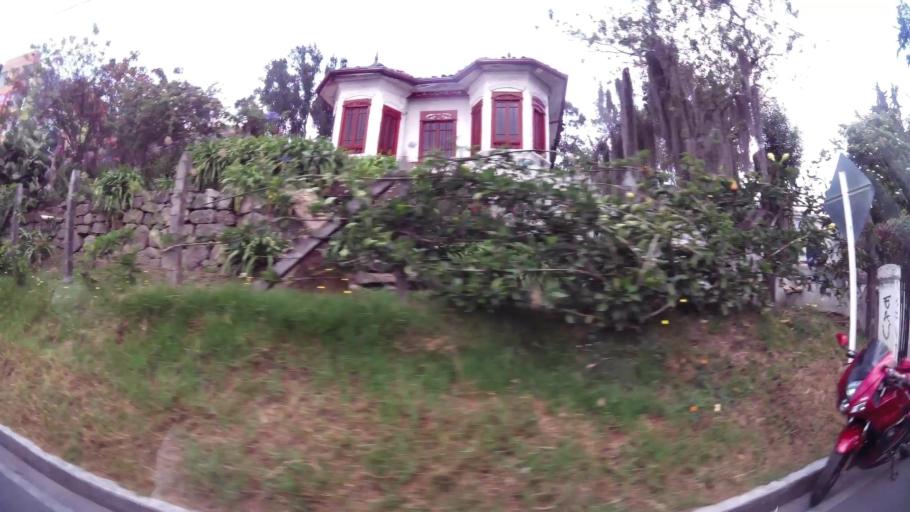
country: CO
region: Cundinamarca
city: Cota
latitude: 4.7380
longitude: -74.0831
